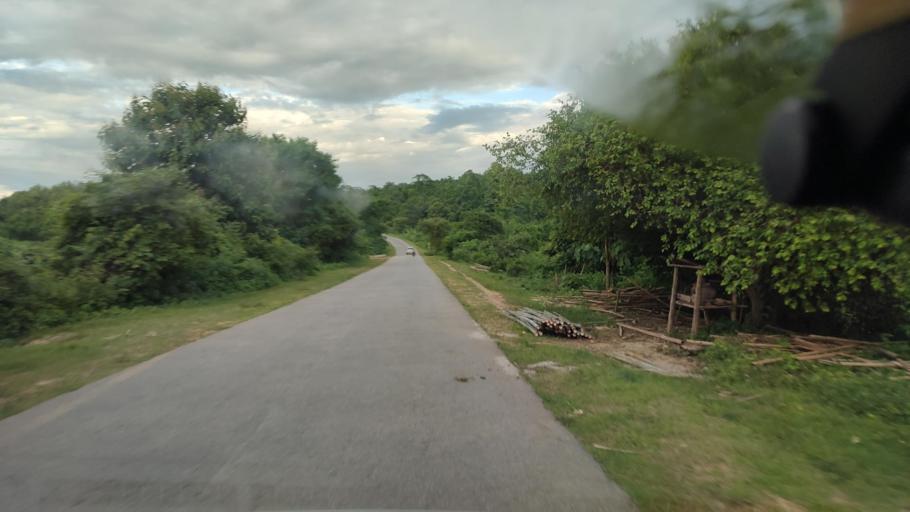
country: MM
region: Mandalay
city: Nay Pyi Taw
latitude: 19.9940
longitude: 95.9346
